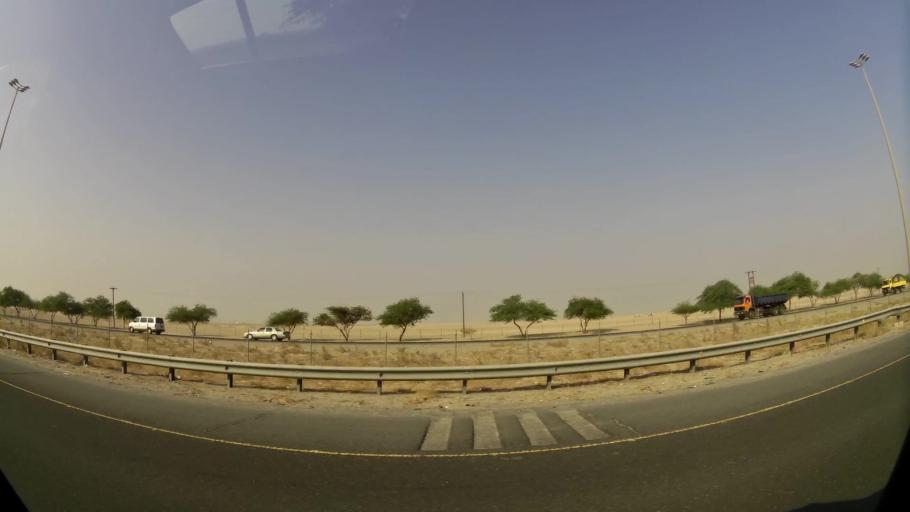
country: KW
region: Al Asimah
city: Ar Rabiyah
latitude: 29.2081
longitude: 47.8845
